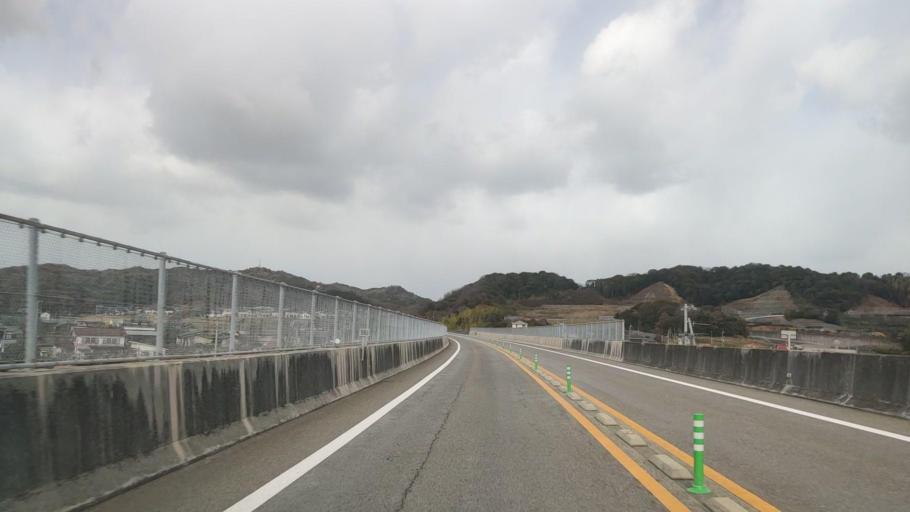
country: JP
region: Ehime
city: Hojo
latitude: 34.0615
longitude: 132.9726
